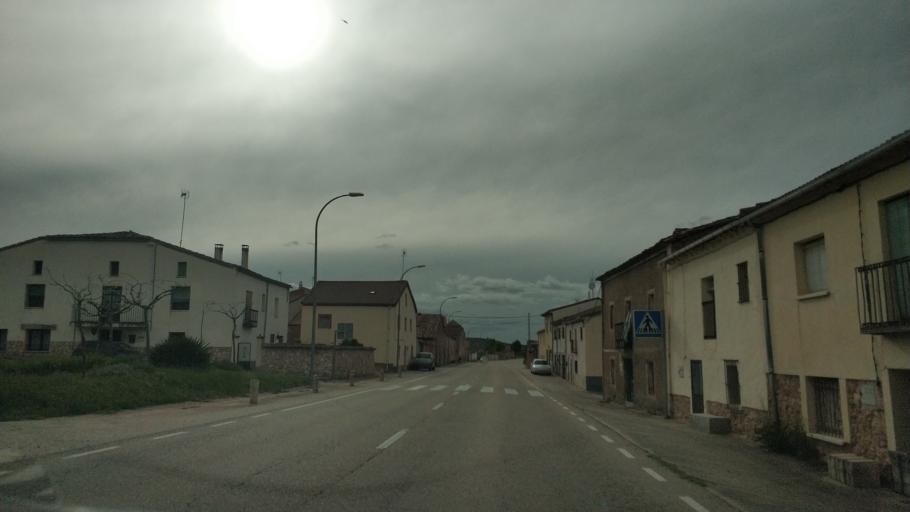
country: ES
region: Castille and Leon
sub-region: Provincia de Soria
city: Valdenebro
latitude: 41.5696
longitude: -3.0087
